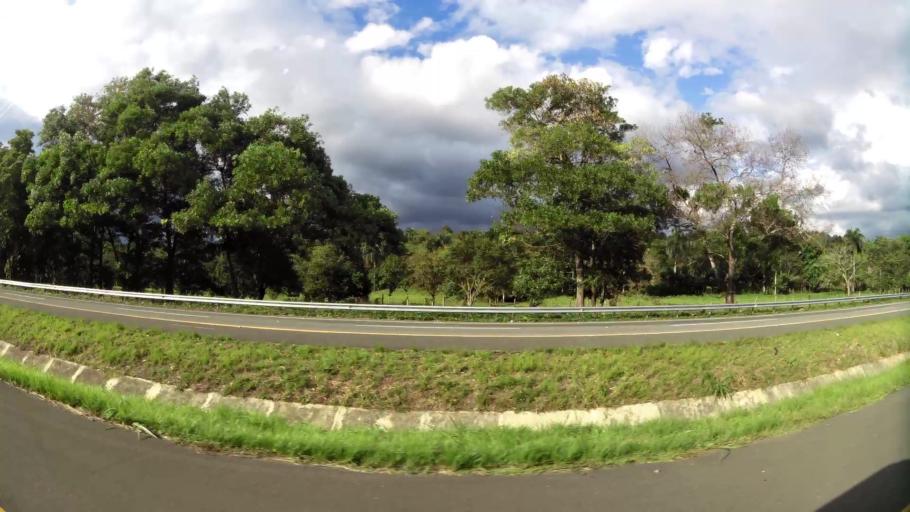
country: DO
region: Monsenor Nouel
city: Piedra Blanca
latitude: 18.8574
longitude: -70.3418
